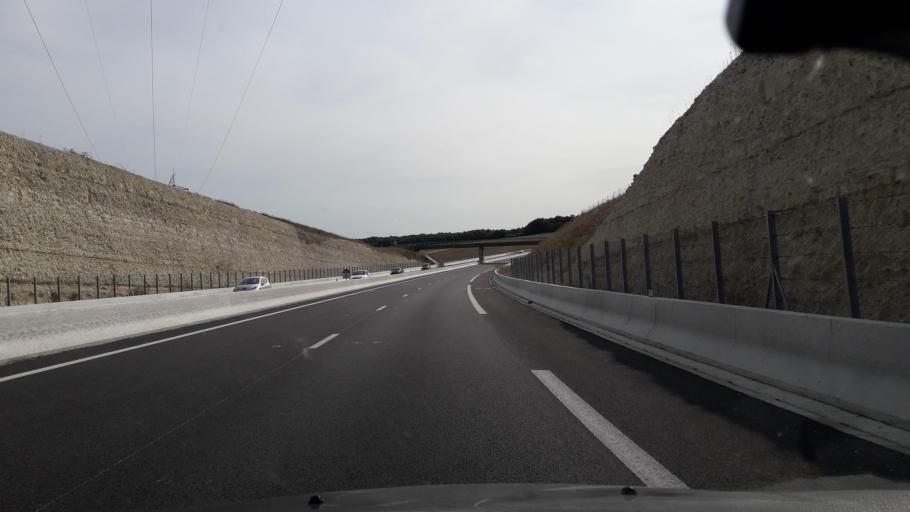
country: FR
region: Poitou-Charentes
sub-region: Departement de la Charente
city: Fleac
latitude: 45.6885
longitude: 0.0829
